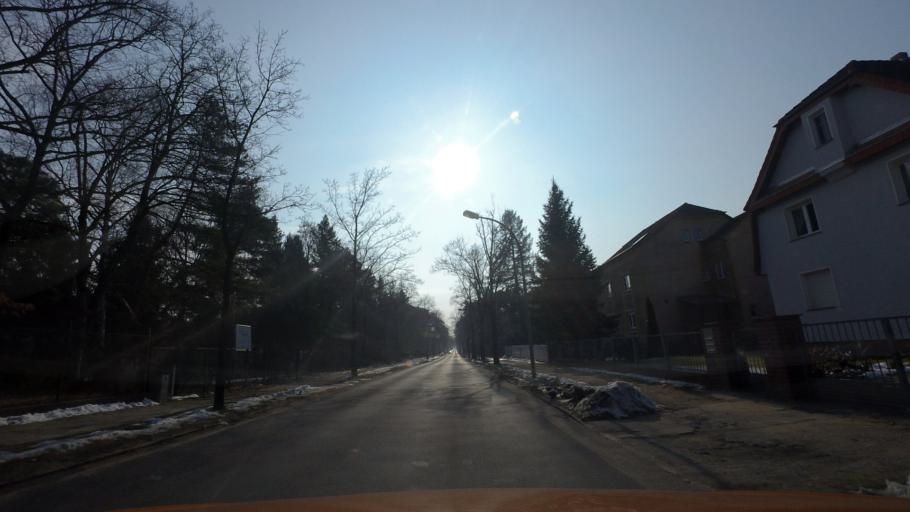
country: DE
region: Brandenburg
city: Am Mellensee
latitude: 52.1758
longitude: 13.4010
